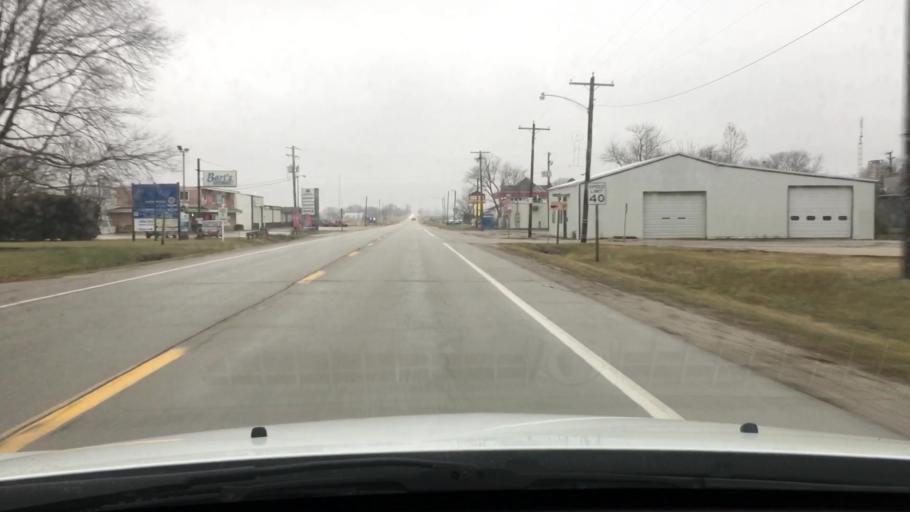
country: US
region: Illinois
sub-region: Livingston County
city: Flanagan
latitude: 40.8711
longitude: -88.8591
